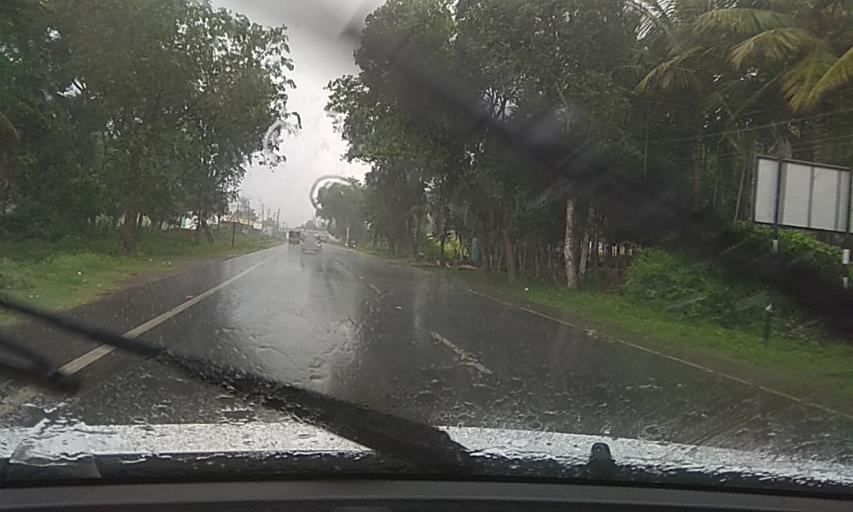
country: IN
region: Karnataka
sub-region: Tumkur
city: Kunigal
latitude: 13.0033
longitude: 77.0226
